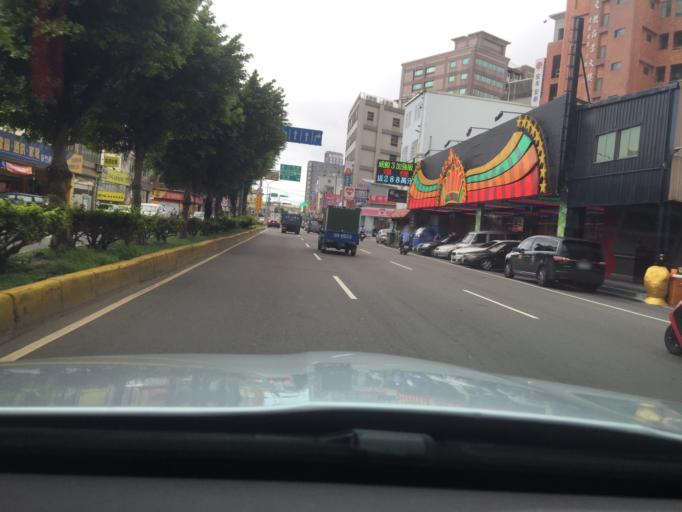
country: TW
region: Taiwan
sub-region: Hsinchu
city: Hsinchu
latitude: 24.8146
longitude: 120.9782
